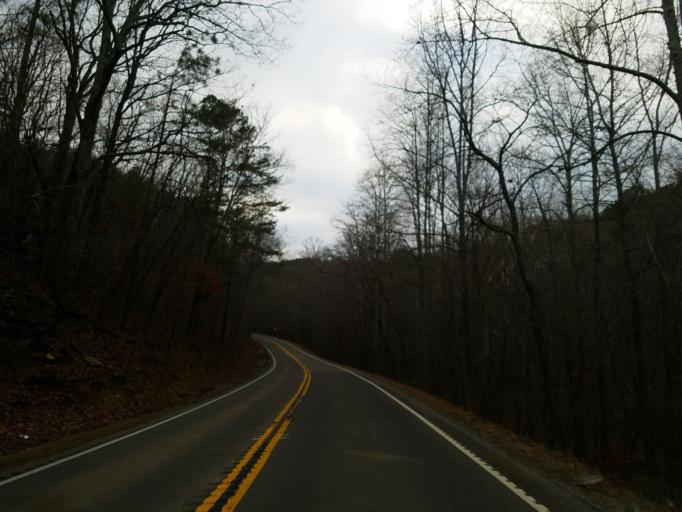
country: US
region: Georgia
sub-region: Bartow County
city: Rydal
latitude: 34.3445
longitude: -84.6390
